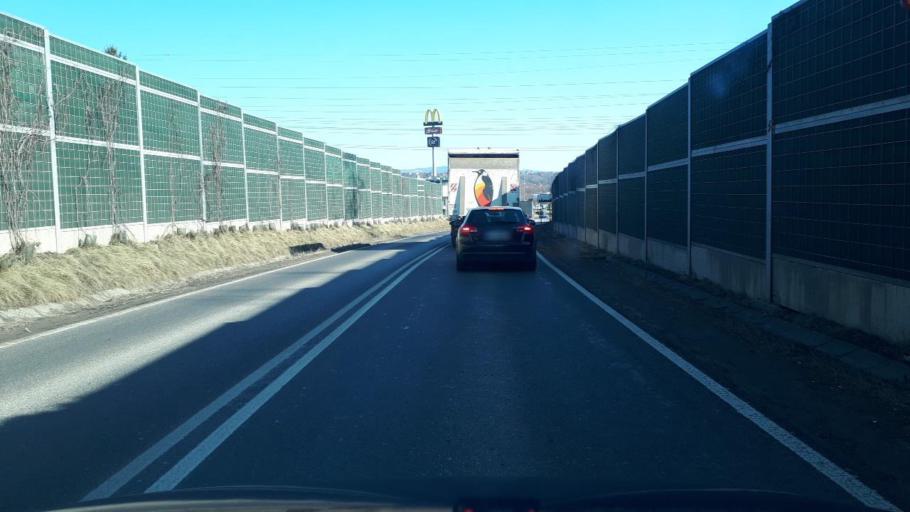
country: PL
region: Silesian Voivodeship
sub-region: Powiat zywiecki
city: Zywiec
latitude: 49.6902
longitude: 19.1791
